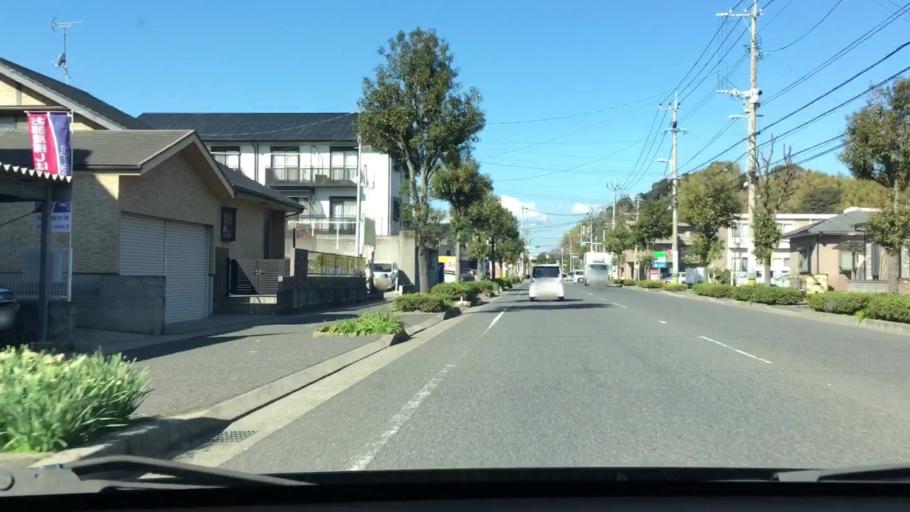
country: JP
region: Kagoshima
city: Kagoshima-shi
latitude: 31.5503
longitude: 130.5309
